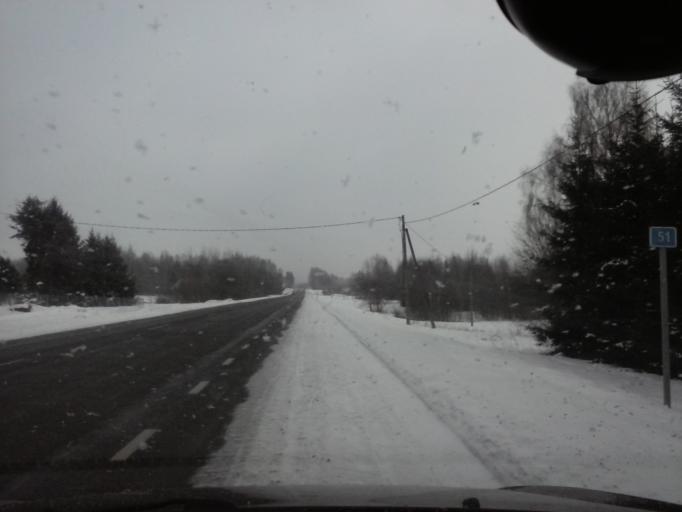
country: EE
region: Viljandimaa
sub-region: Viljandi linn
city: Viljandi
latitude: 58.3521
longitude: 25.5609
